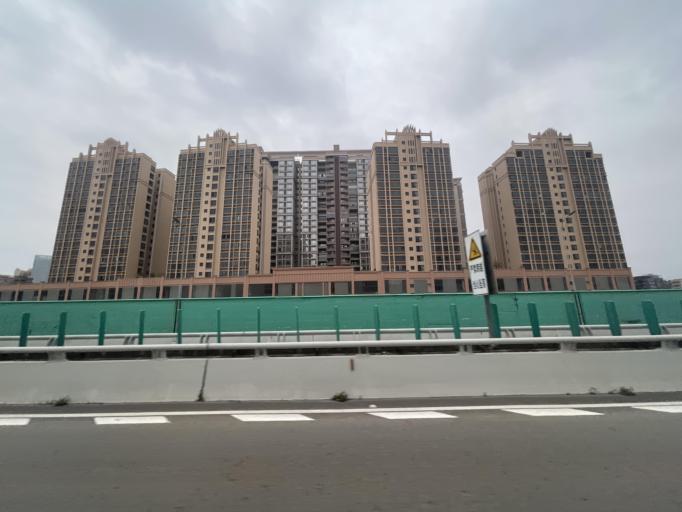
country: CN
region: Guangdong
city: Humen
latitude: 22.8071
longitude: 113.6852
